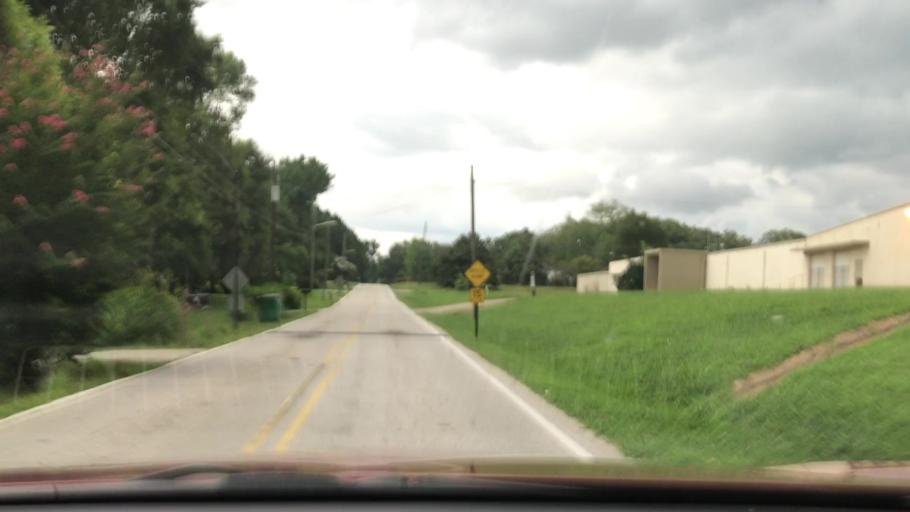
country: US
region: Georgia
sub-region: Barrow County
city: Winder
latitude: 33.9903
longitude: -83.7355
